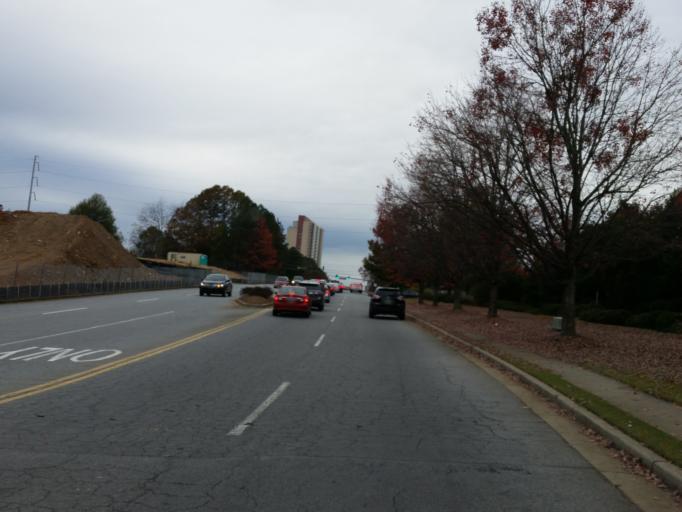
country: US
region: Georgia
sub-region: DeKalb County
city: Dunwoody
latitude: 33.9318
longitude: -84.3351
